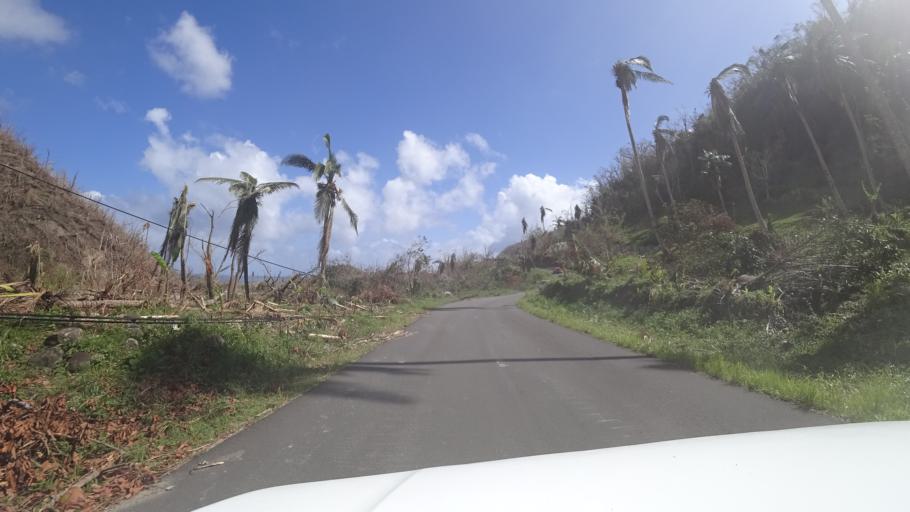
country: DM
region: Saint Patrick
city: Berekua
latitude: 15.2524
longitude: -61.3172
